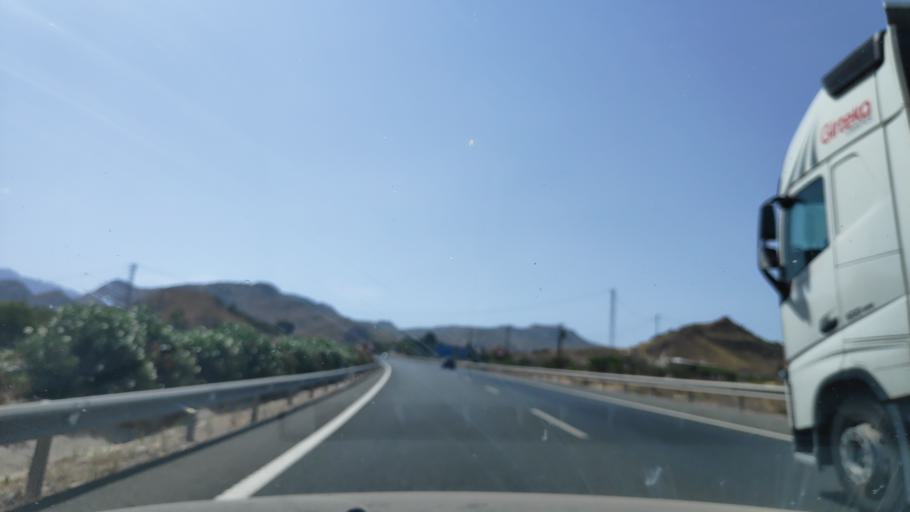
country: ES
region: Murcia
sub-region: Murcia
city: Archena
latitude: 38.1526
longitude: -1.2851
